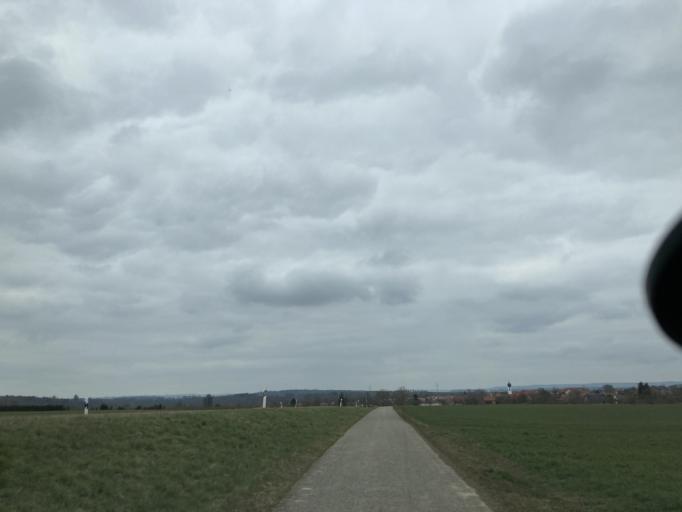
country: DE
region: Baden-Wuerttemberg
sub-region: Tuebingen Region
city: Hirrlingen
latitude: 48.4431
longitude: 8.8786
